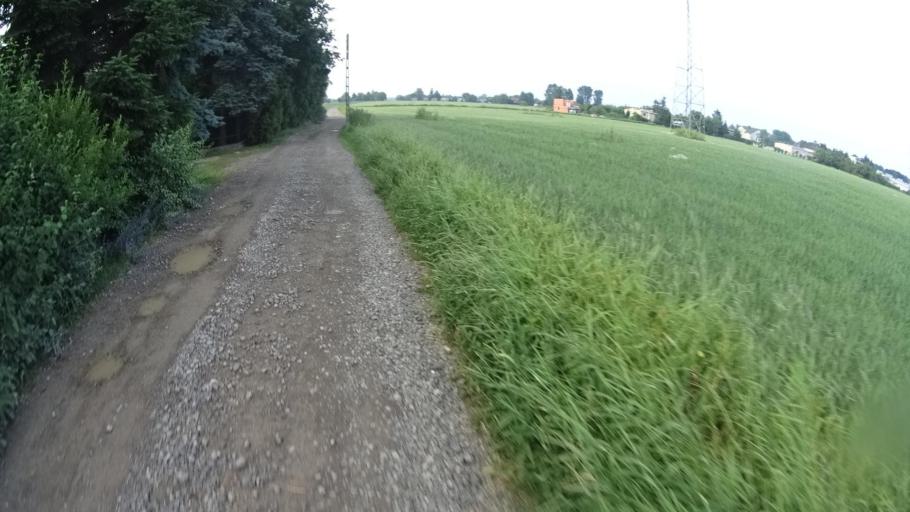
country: PL
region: Masovian Voivodeship
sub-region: Powiat warszawski zachodni
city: Babice
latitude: 52.2203
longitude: 20.8549
